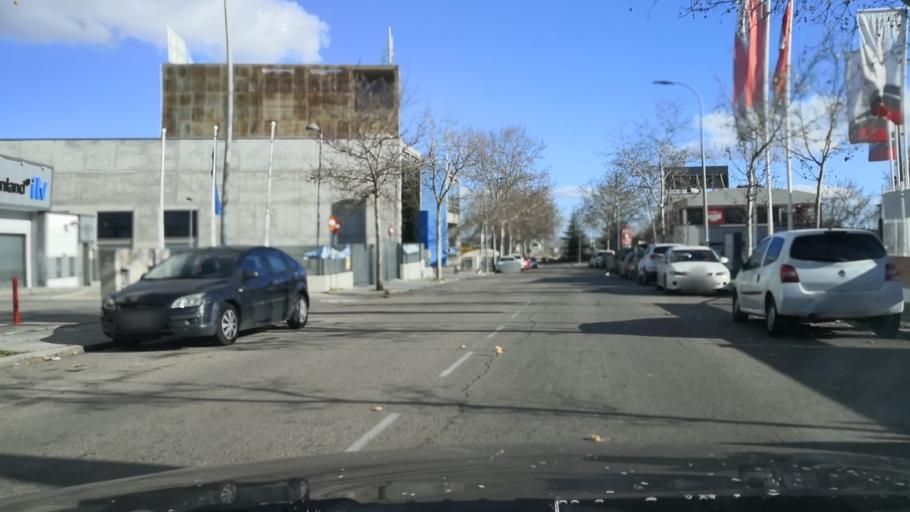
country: ES
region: Madrid
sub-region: Provincia de Madrid
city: San Sebastian de los Reyes
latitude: 40.5477
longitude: -3.6122
